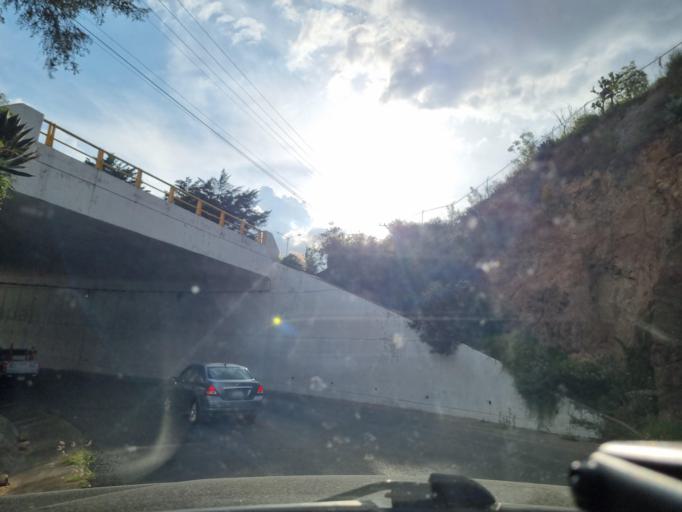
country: MX
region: Mexico
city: Ciudad Lopez Mateos
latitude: 19.5490
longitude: -99.2816
